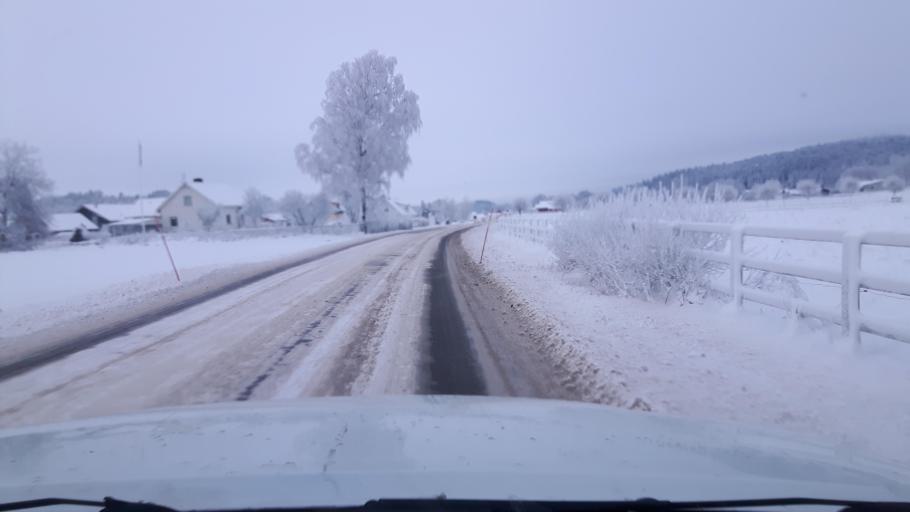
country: SE
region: Halland
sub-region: Kungsbacka Kommun
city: Fjaeras kyrkby
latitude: 57.4682
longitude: 12.1670
